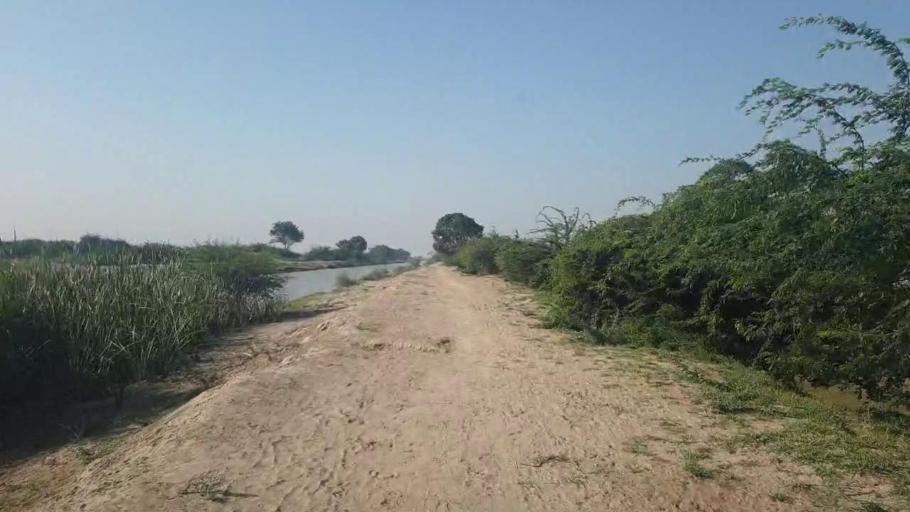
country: PK
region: Sindh
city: Badin
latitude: 24.7056
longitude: 68.8859
